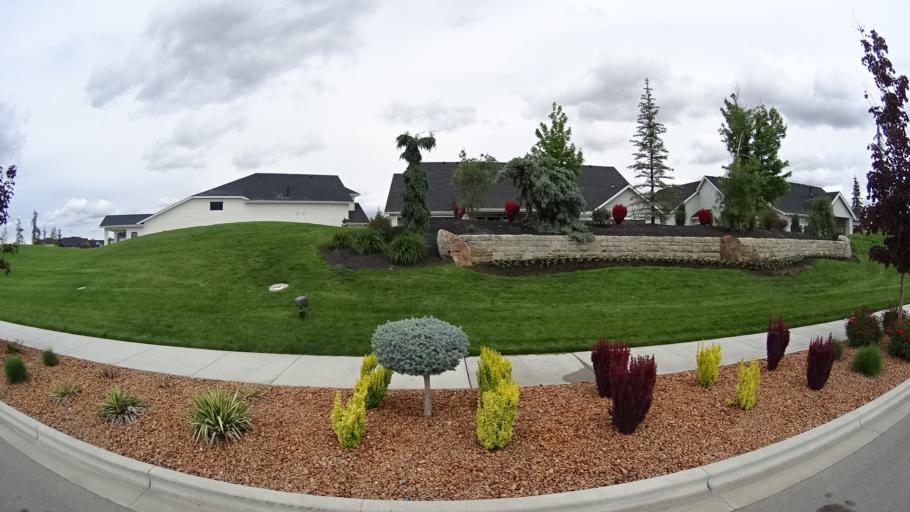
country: US
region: Idaho
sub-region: Ada County
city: Star
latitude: 43.7030
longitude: -116.4380
